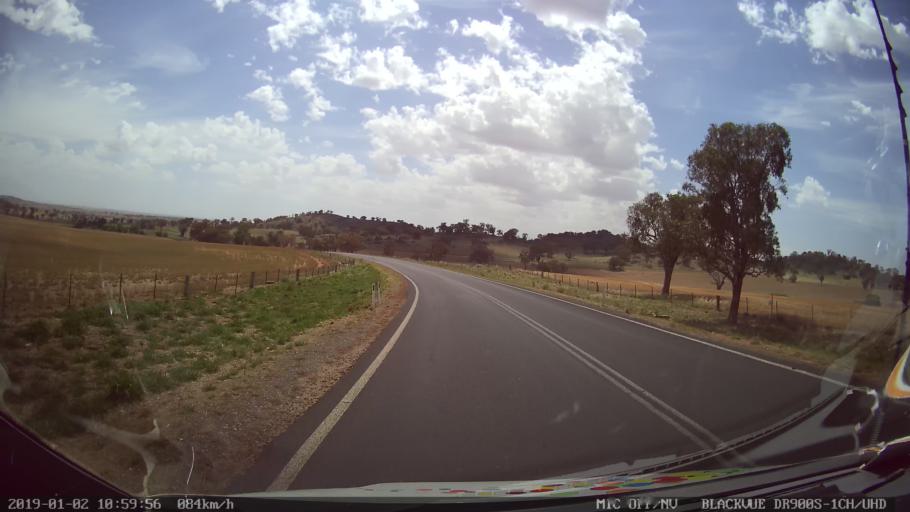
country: AU
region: New South Wales
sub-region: Cootamundra
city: Cootamundra
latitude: -34.6104
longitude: 148.3114
